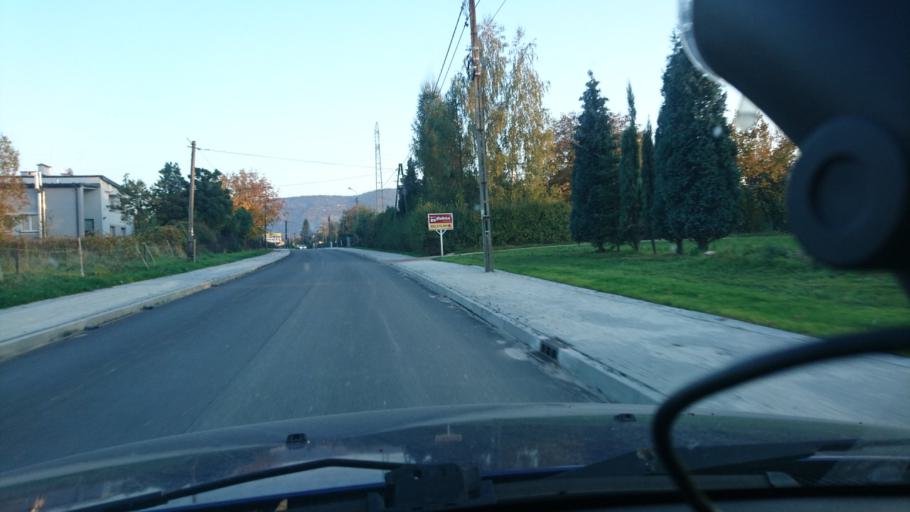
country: PL
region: Silesian Voivodeship
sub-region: Powiat bielski
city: Kozy
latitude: 49.8566
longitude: 19.1350
